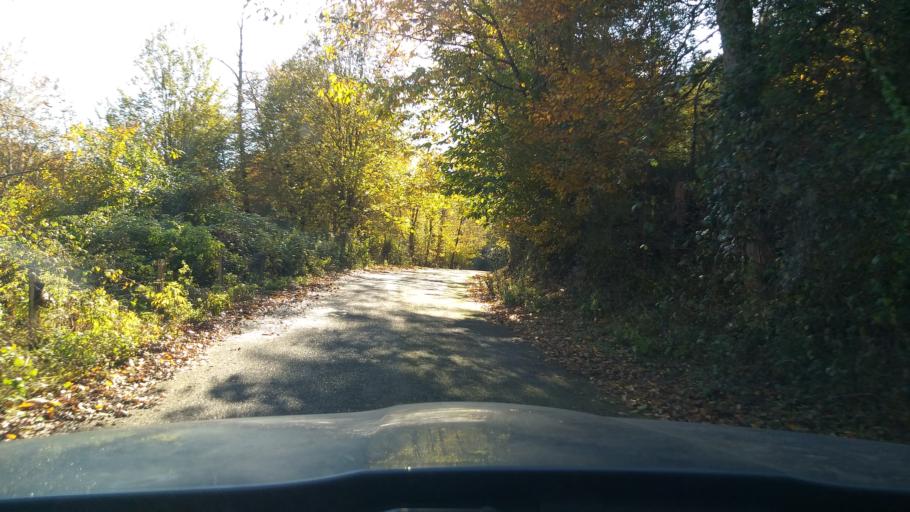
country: GE
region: Abkhazia
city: Bich'vinta
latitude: 43.1839
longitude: 40.4544
